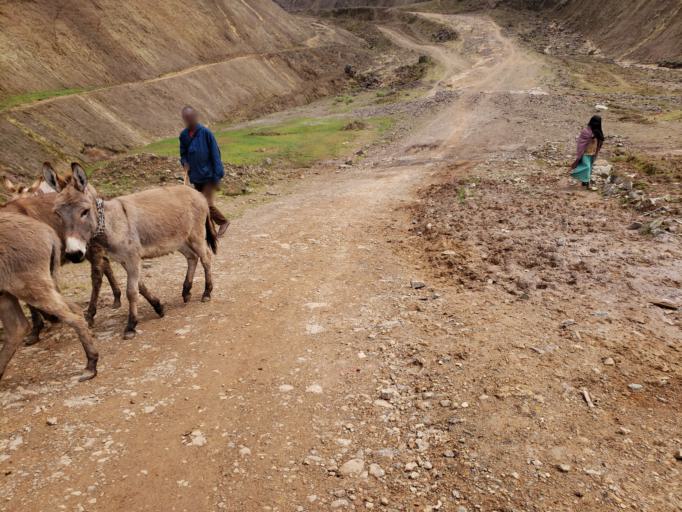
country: ET
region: Oromiya
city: Dodola
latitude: 6.6524
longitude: 39.3616
